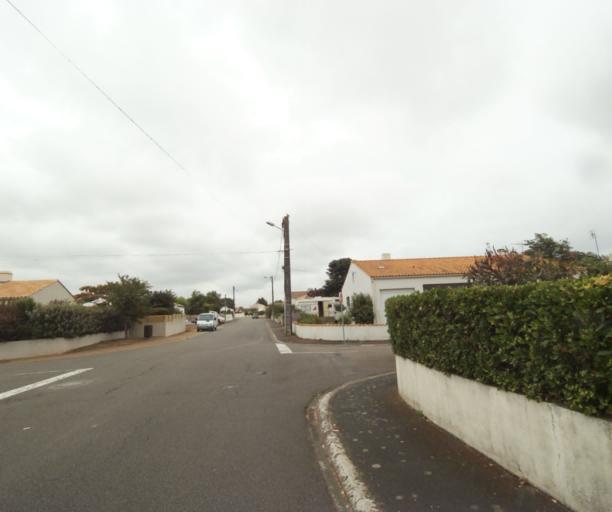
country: FR
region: Pays de la Loire
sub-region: Departement de la Vendee
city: Chateau-d'Olonne
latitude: 46.5026
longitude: -1.7546
